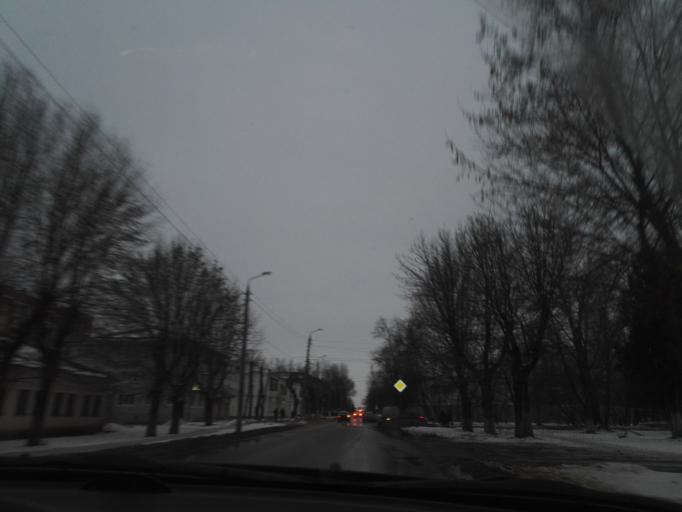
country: RU
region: Tula
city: Novomoskovsk
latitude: 54.0091
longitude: 38.3004
